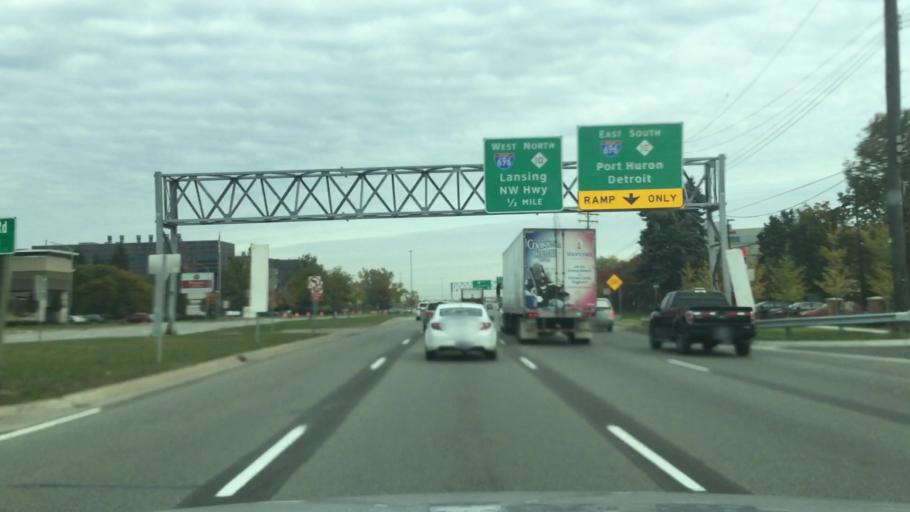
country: US
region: Michigan
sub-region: Oakland County
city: Bingham Farms
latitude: 42.4827
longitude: -83.2853
